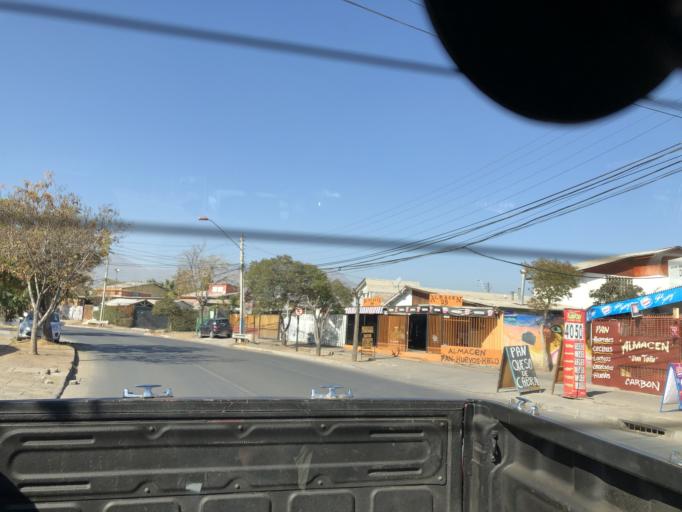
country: CL
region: Santiago Metropolitan
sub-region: Provincia de Cordillera
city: Puente Alto
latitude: -33.5659
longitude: -70.5742
